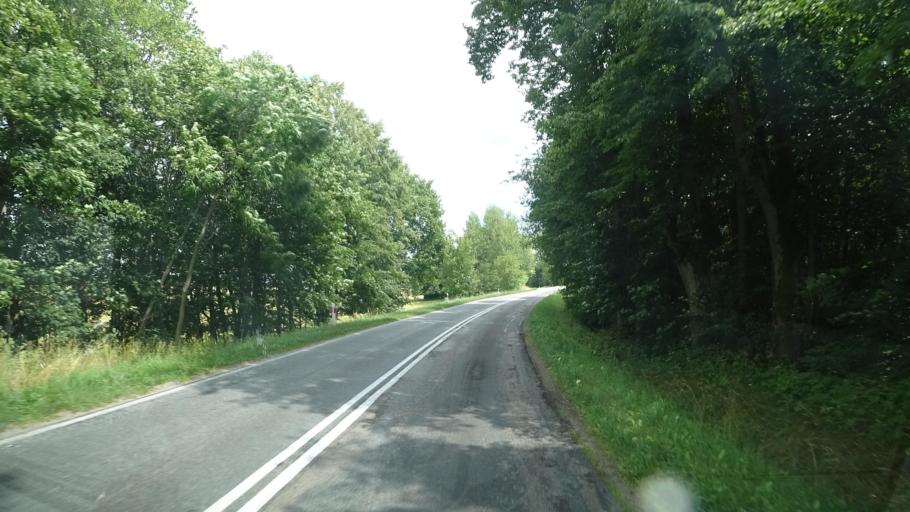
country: PL
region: Warmian-Masurian Voivodeship
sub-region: Powiat goldapski
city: Banie Mazurskie
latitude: 54.2118
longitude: 22.1758
